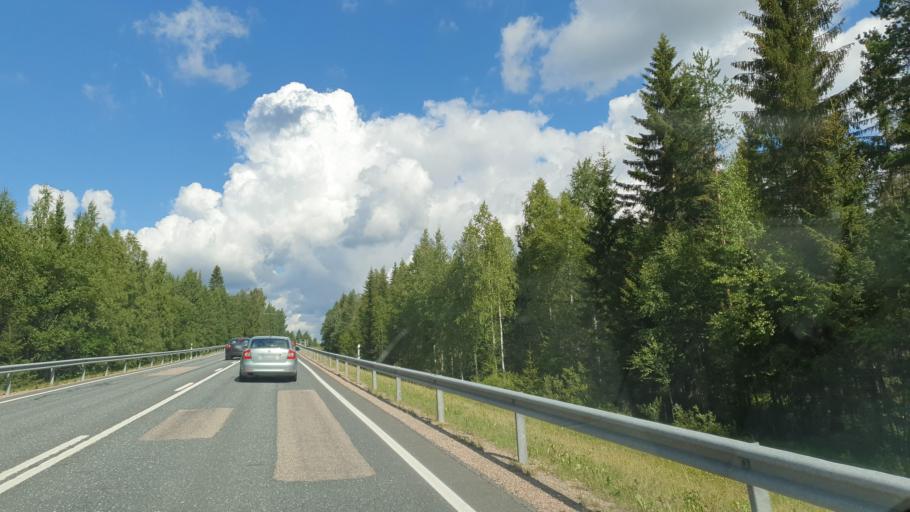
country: FI
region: Kainuu
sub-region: Kajaani
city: Kajaani
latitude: 64.0497
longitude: 27.4518
